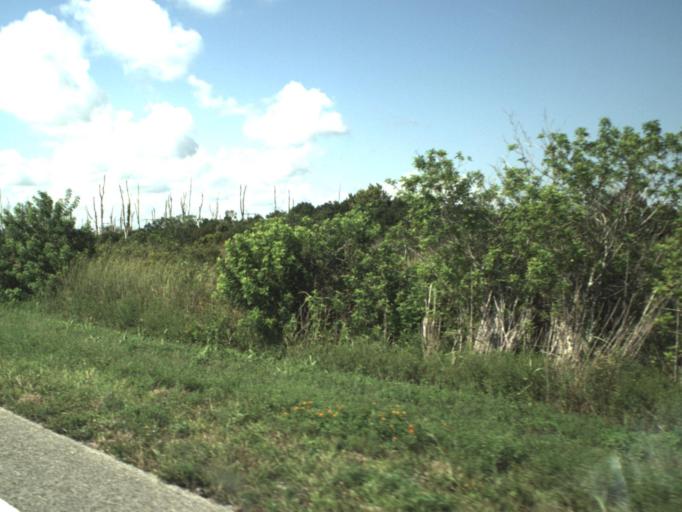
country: US
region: Florida
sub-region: Broward County
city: Weston
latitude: 26.0945
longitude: -80.4345
